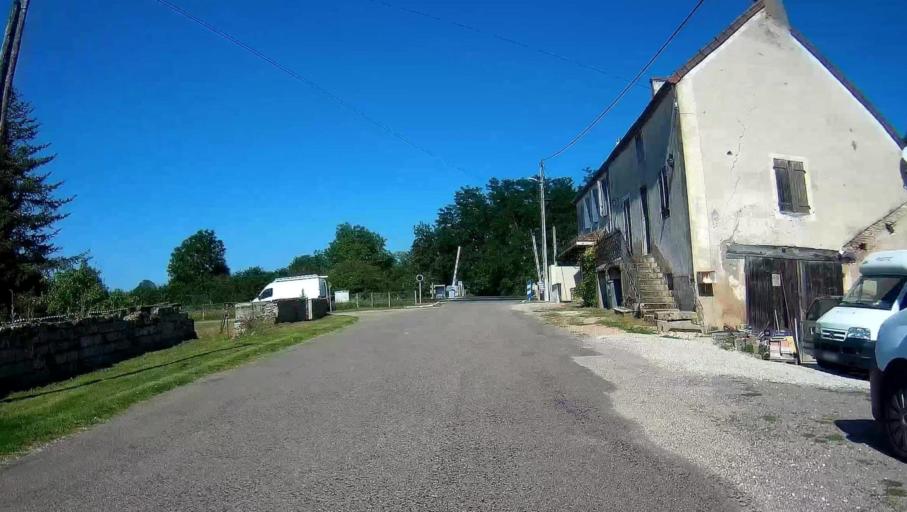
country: FR
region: Bourgogne
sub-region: Departement de Saone-et-Loire
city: Saint-Leger-sur-Dheune
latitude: 46.8254
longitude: 4.5961
